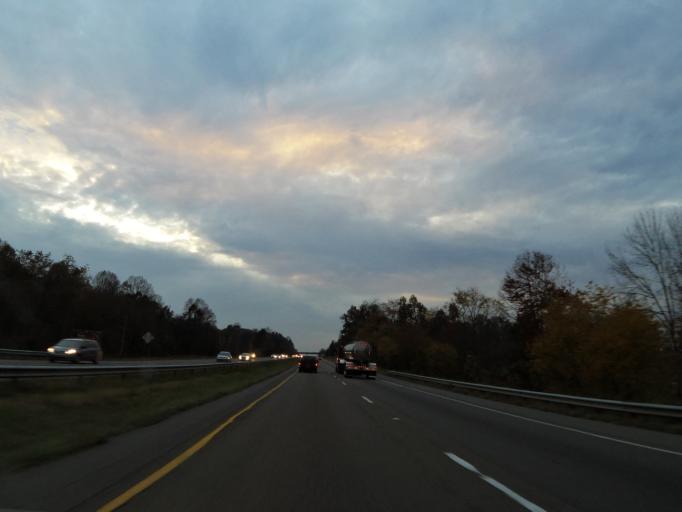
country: US
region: North Carolina
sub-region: Burke County
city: Salem
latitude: 35.7179
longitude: -81.7253
